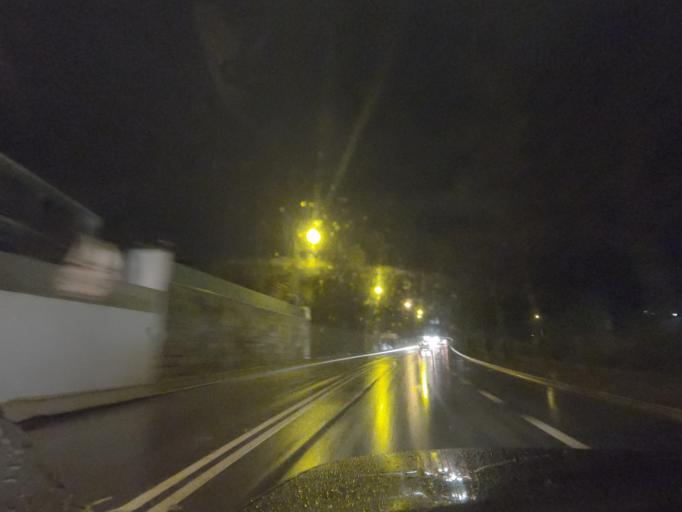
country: PT
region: Vila Real
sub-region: Vila Real
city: Vila Real
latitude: 41.3050
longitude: -7.7338
